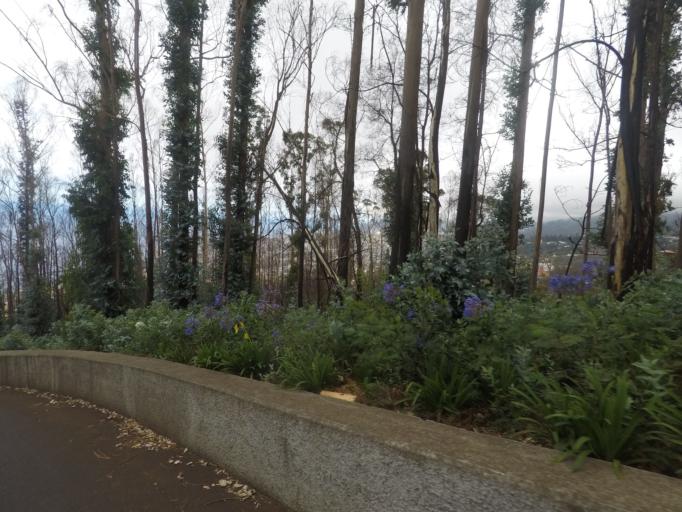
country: PT
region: Madeira
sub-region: Funchal
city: Nossa Senhora do Monte
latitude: 32.6680
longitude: -16.8846
